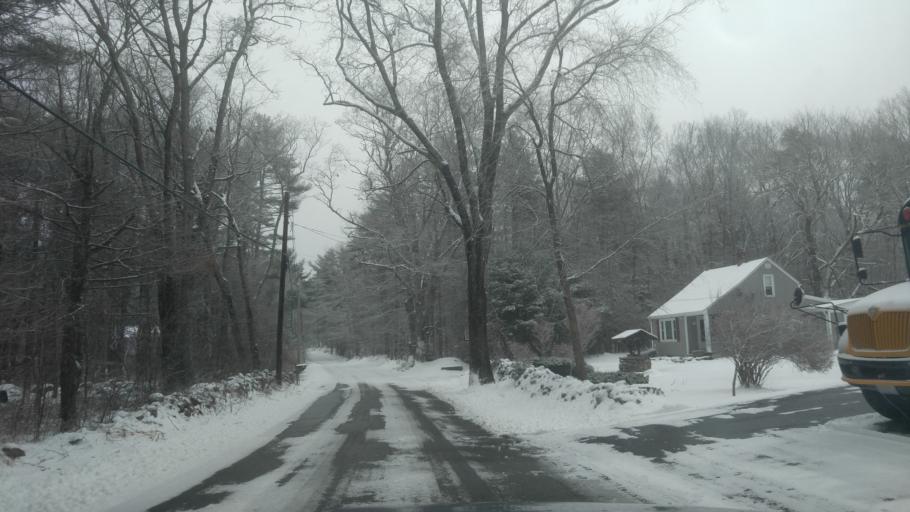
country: US
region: Rhode Island
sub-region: Providence County
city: Foster
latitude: 41.8247
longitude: -71.7277
